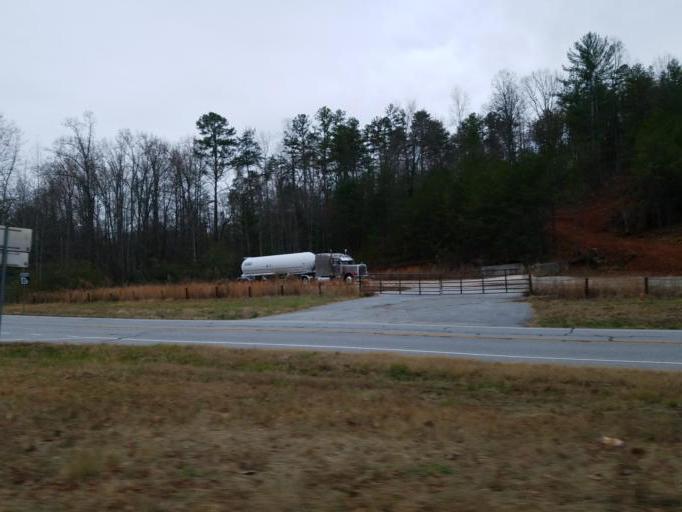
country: US
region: Georgia
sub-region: Dawson County
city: Dawsonville
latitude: 34.5120
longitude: -84.2283
